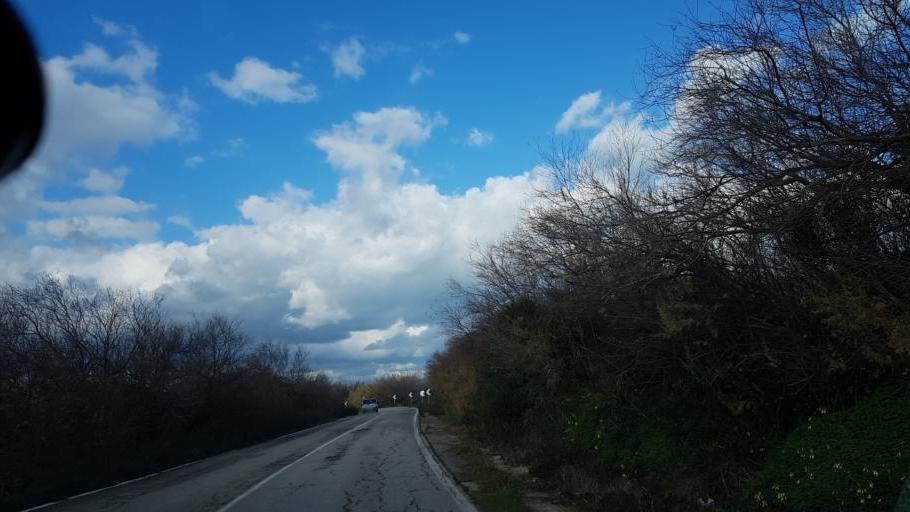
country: IT
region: Apulia
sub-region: Provincia di Brindisi
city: Materdomini
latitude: 40.6792
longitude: 17.9241
